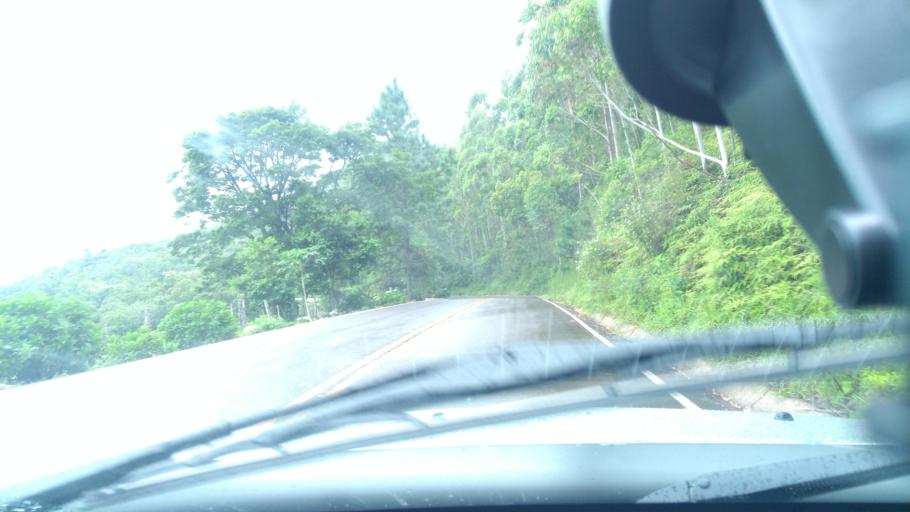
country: BR
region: Rio Grande do Sul
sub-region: Torres
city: Torres
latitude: -29.1886
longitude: -49.9860
